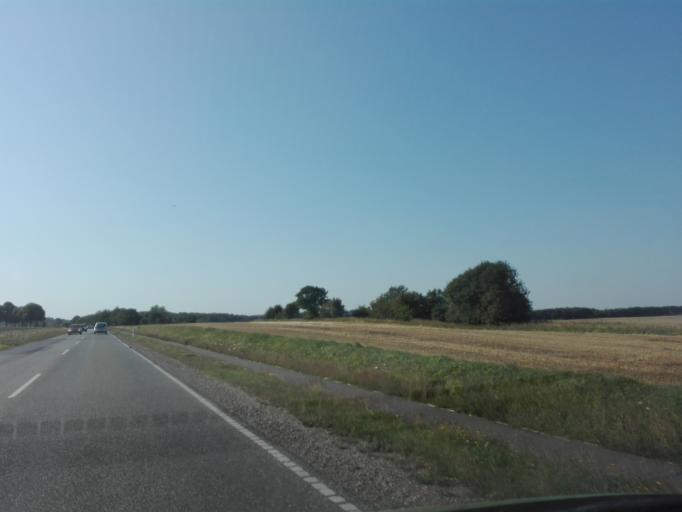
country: DK
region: Central Jutland
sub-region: Odder Kommune
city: Odder
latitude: 55.9624
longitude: 10.1738
